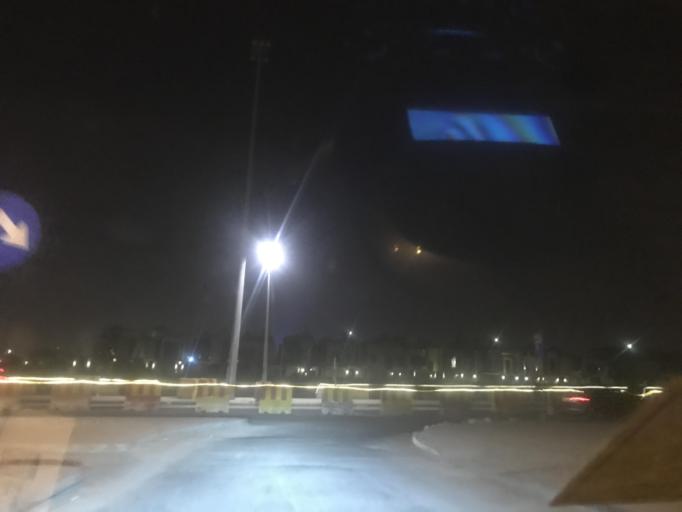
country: SA
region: Ar Riyad
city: Riyadh
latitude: 24.7988
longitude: 46.5943
